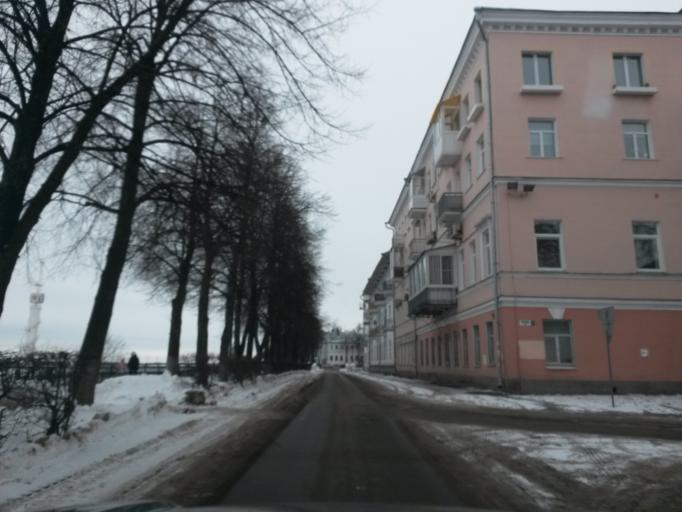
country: RU
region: Jaroslavl
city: Yaroslavl
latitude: 57.6344
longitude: 39.8920
